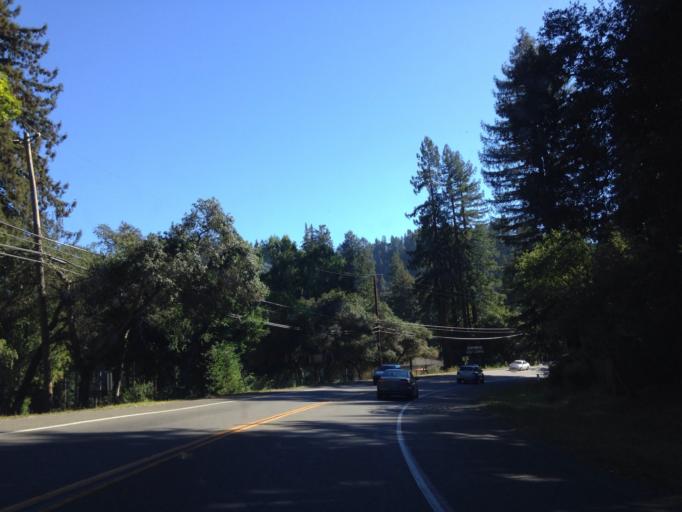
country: US
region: California
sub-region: Sonoma County
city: Monte Rio
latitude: 38.4796
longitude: -122.9969
